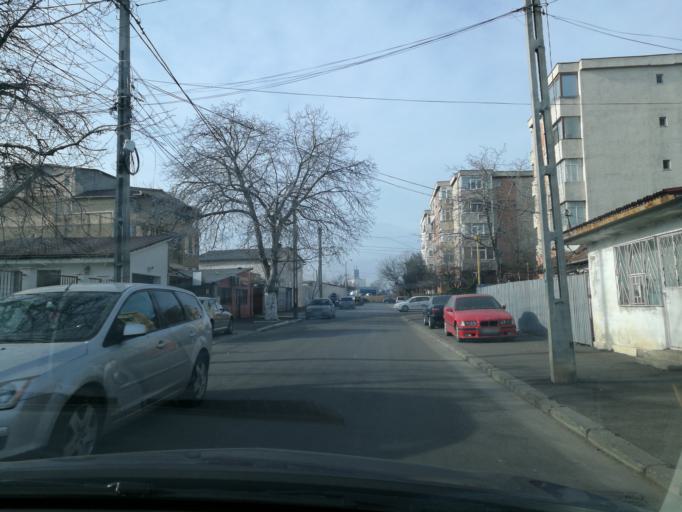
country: RO
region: Constanta
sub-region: Municipiul Constanta
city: Constanta
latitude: 44.1754
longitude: 28.6105
